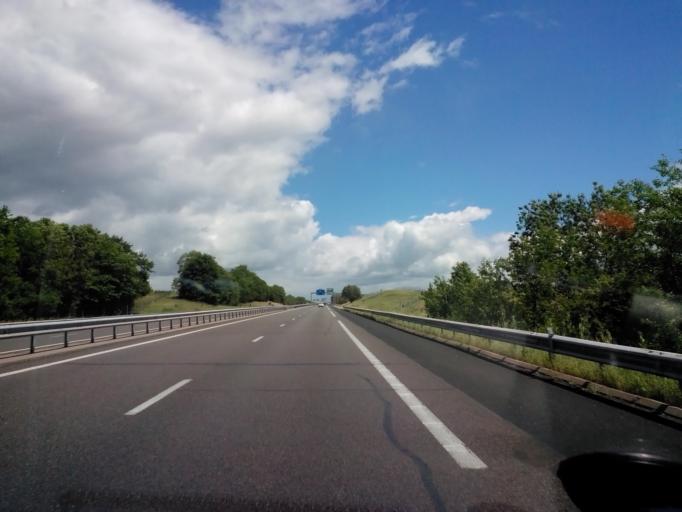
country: FR
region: Lorraine
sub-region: Departement des Vosges
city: Bulgneville
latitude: 48.2171
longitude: 5.8282
